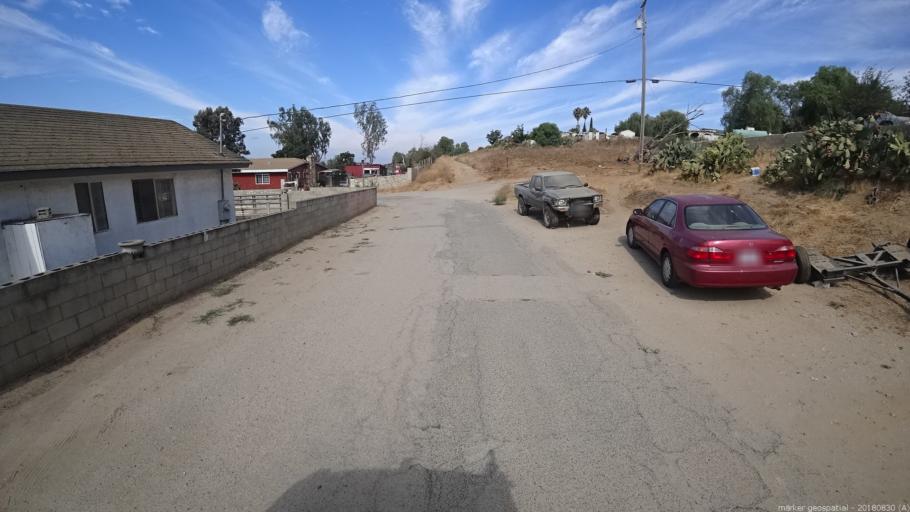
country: US
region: California
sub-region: Monterey County
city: King City
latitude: 36.1306
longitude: -121.0227
